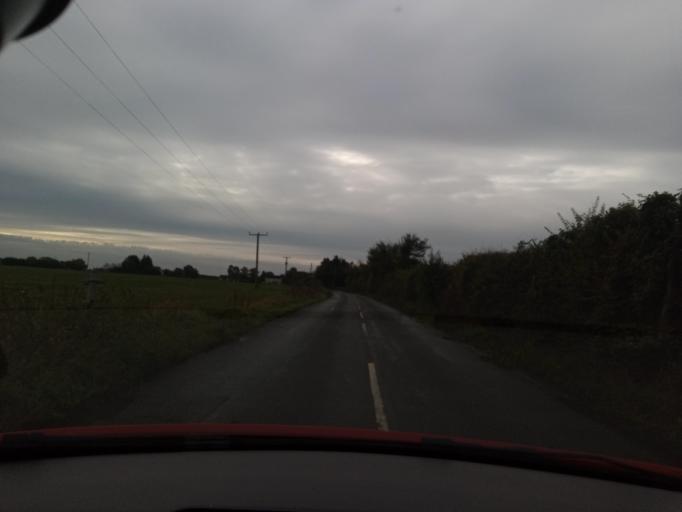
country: GB
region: England
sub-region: Essex
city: West Mersea
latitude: 51.7883
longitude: 0.9389
